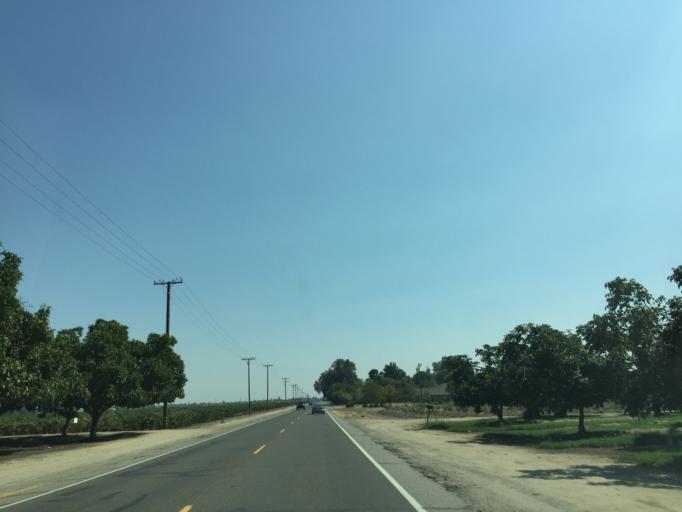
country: US
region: California
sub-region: Kings County
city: Lucerne
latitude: 36.3688
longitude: -119.6730
